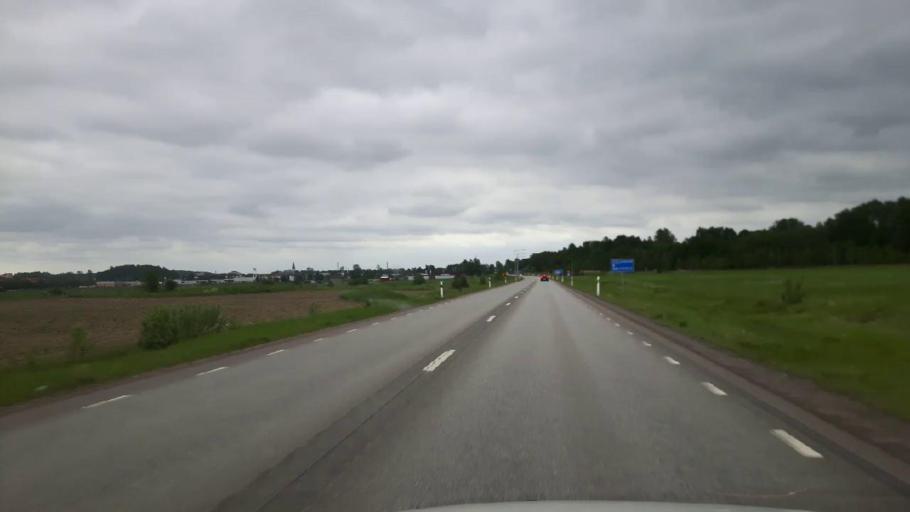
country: SE
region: Vaestmanland
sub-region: Kopings Kommun
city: Koping
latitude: 59.5308
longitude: 15.9577
